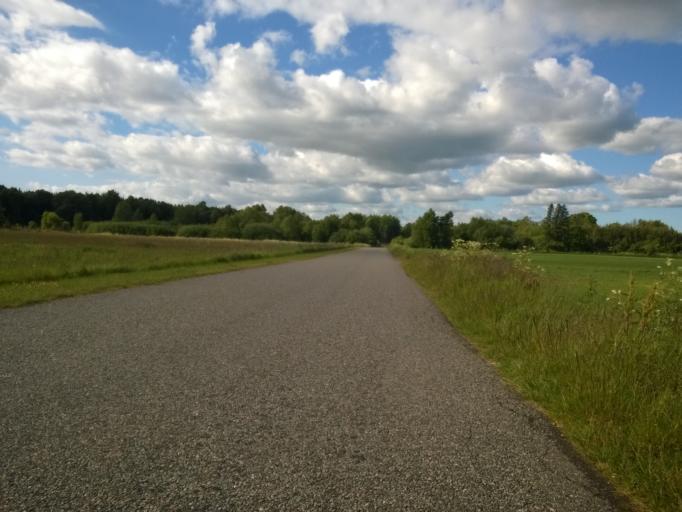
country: DK
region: Central Jutland
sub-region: Holstebro Kommune
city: Vinderup
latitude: 56.5065
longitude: 8.8477
